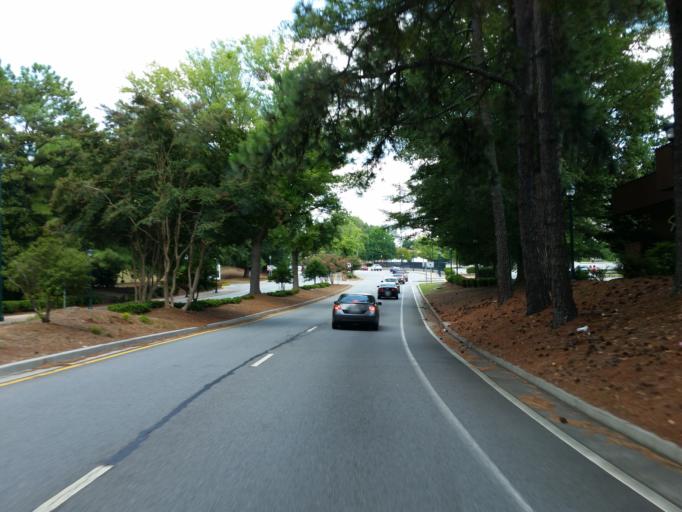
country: US
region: Georgia
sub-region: DeKalb County
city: Dunwoody
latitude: 33.9268
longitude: -84.3400
